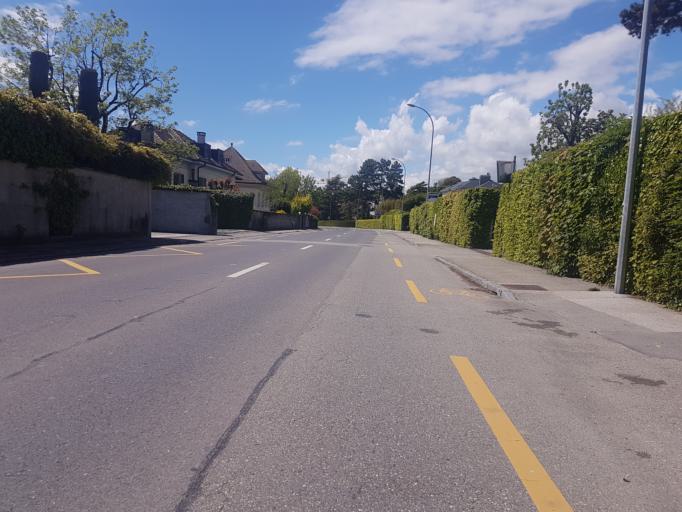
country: CH
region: Vaud
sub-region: Nyon District
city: Prangins
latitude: 46.3880
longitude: 6.2479
